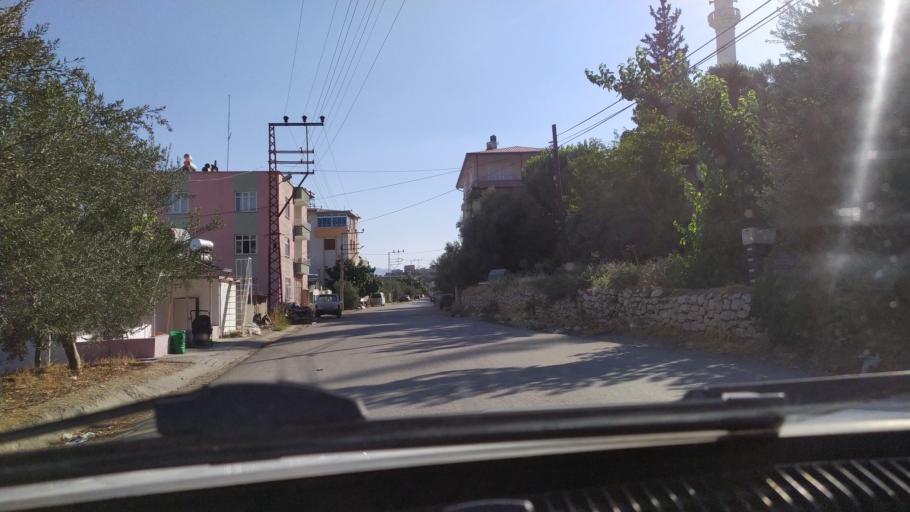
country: TR
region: Mersin
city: Mut
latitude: 36.6480
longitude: 33.4335
